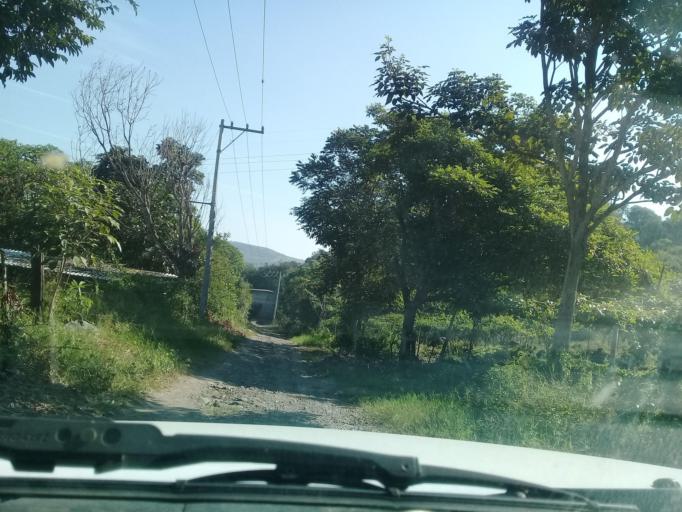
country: MX
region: Veracruz
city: Actopan
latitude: 19.4967
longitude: -96.6105
